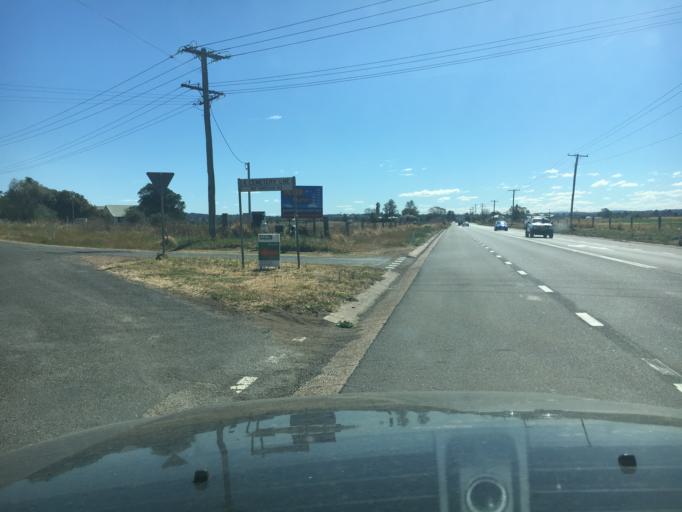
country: AU
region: New South Wales
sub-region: Singleton
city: Singleton
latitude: -32.5882
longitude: 151.1929
